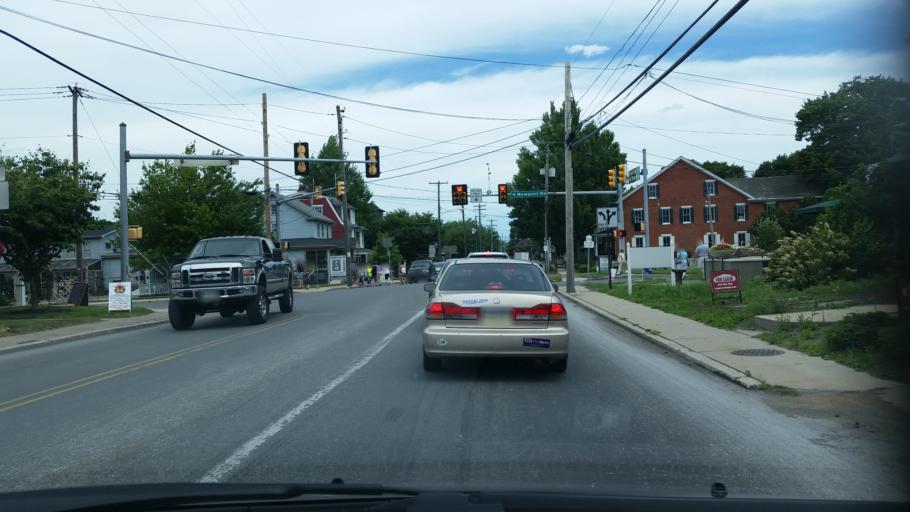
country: US
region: Pennsylvania
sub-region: Lancaster County
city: Intercourse
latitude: 40.0389
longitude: -76.1115
